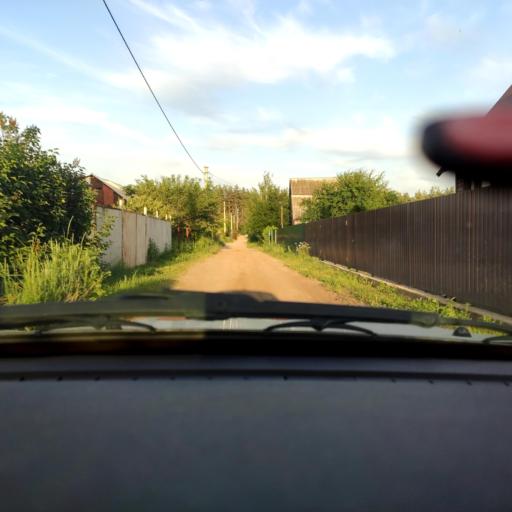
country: RU
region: Voronezj
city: Podgornoye
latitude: 51.8345
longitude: 39.1922
